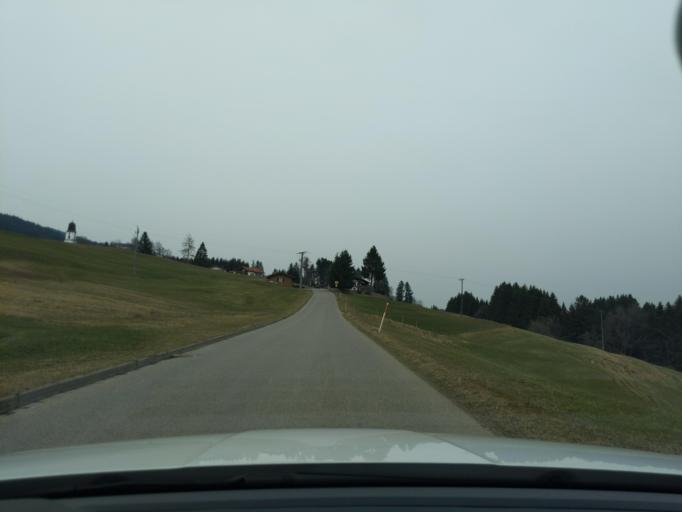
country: DE
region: Bavaria
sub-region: Swabia
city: Ofterschwang
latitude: 47.4926
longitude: 10.2407
